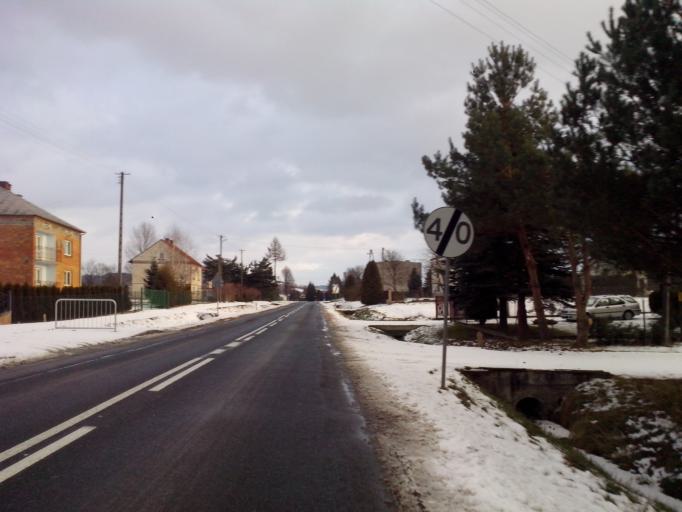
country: PL
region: Subcarpathian Voivodeship
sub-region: Powiat strzyzowski
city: Strzyzow
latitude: 49.8429
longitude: 21.8164
